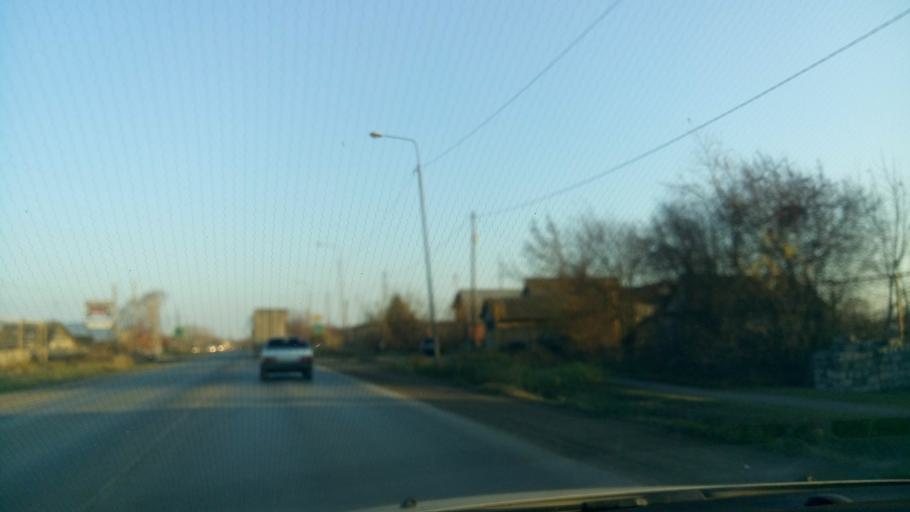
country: RU
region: Sverdlovsk
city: Bogdanovich
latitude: 56.7588
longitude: 62.0786
